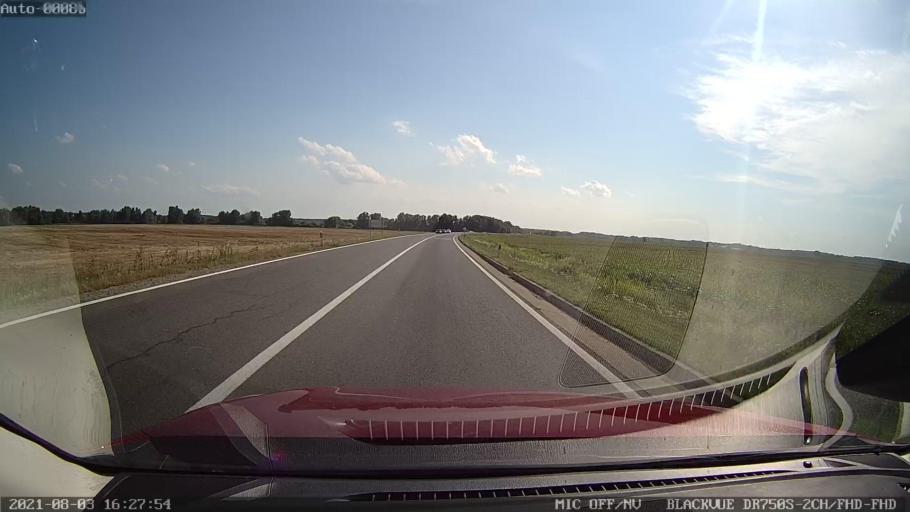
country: HR
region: Osjecko-Baranjska
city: Darda
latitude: 45.6148
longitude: 18.6733
